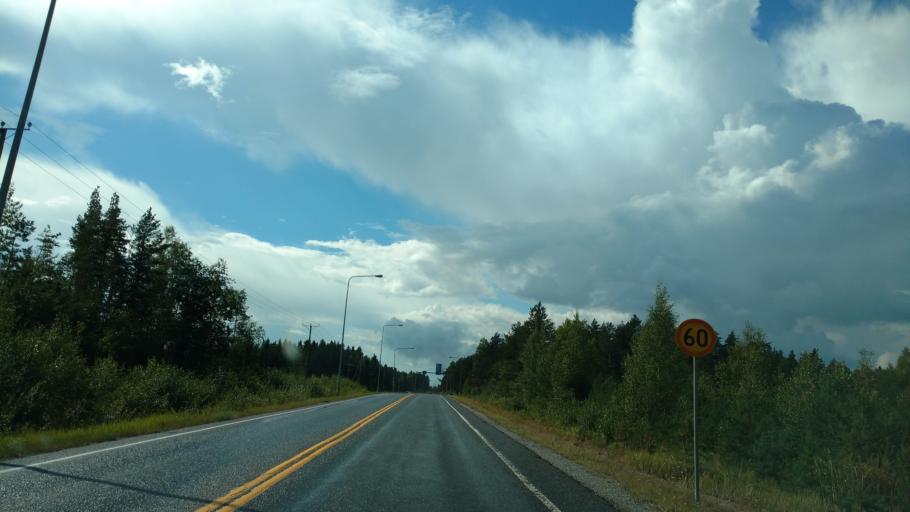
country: FI
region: Varsinais-Suomi
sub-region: Turku
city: Paimio
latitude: 60.4212
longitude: 22.7328
